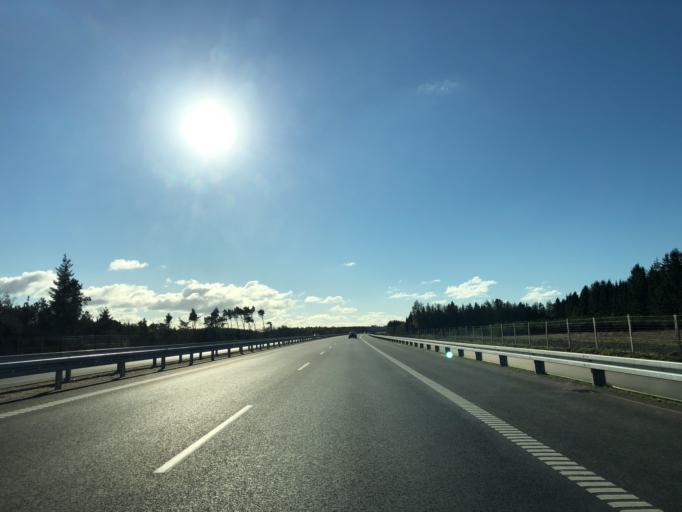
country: DK
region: Central Jutland
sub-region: Herning Kommune
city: Avlum
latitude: 56.3333
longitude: 8.7368
